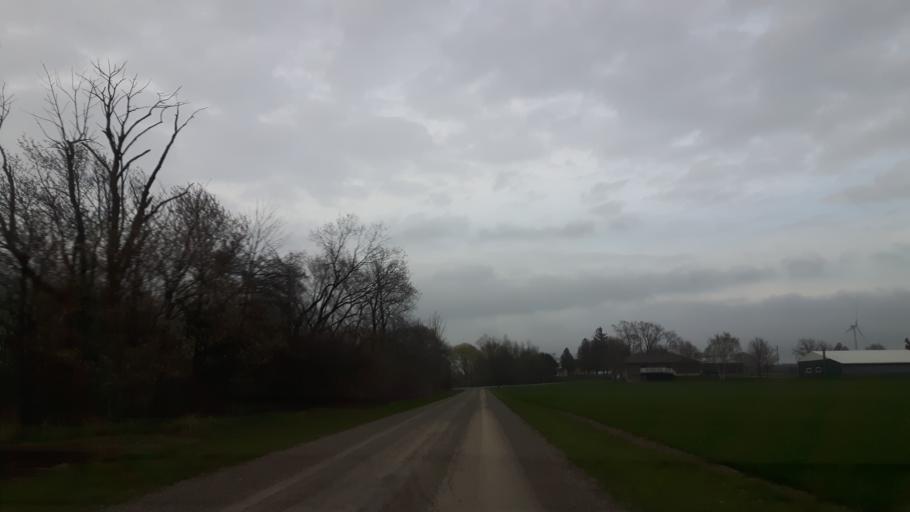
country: CA
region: Ontario
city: Bluewater
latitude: 43.5087
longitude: -81.6716
